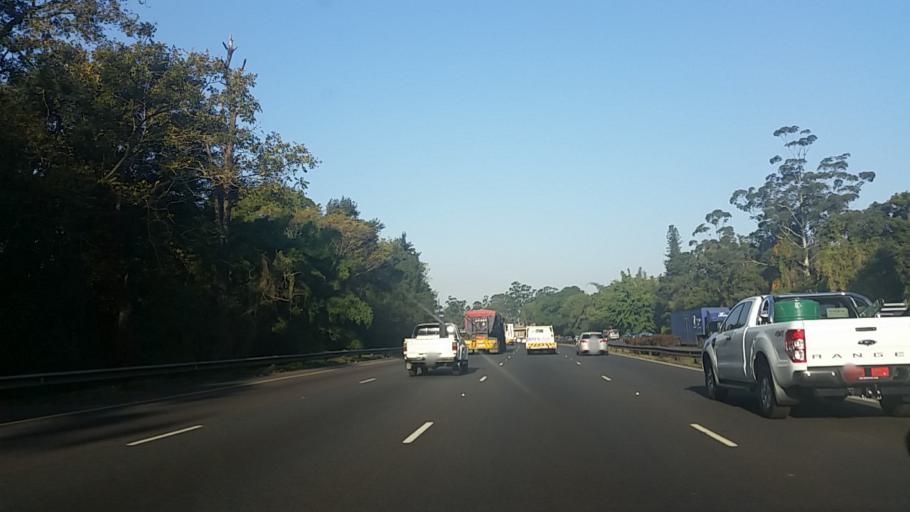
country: ZA
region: KwaZulu-Natal
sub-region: eThekwini Metropolitan Municipality
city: Berea
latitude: -29.8387
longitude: 30.9114
